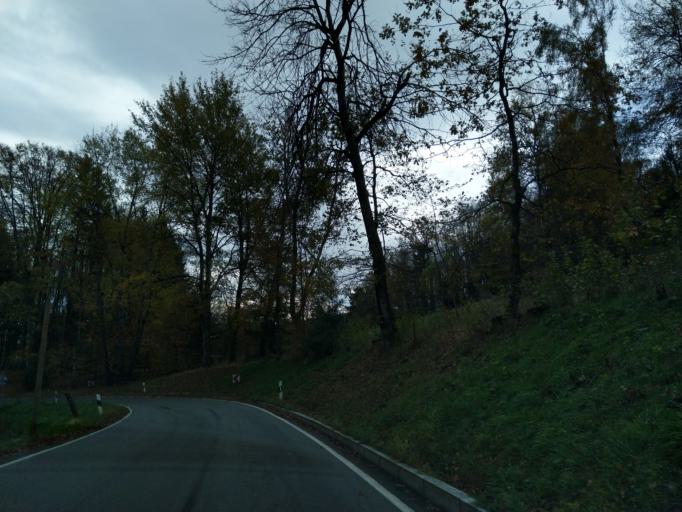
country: DE
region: Bavaria
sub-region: Lower Bavaria
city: Zenting
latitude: 48.7958
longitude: 13.2372
